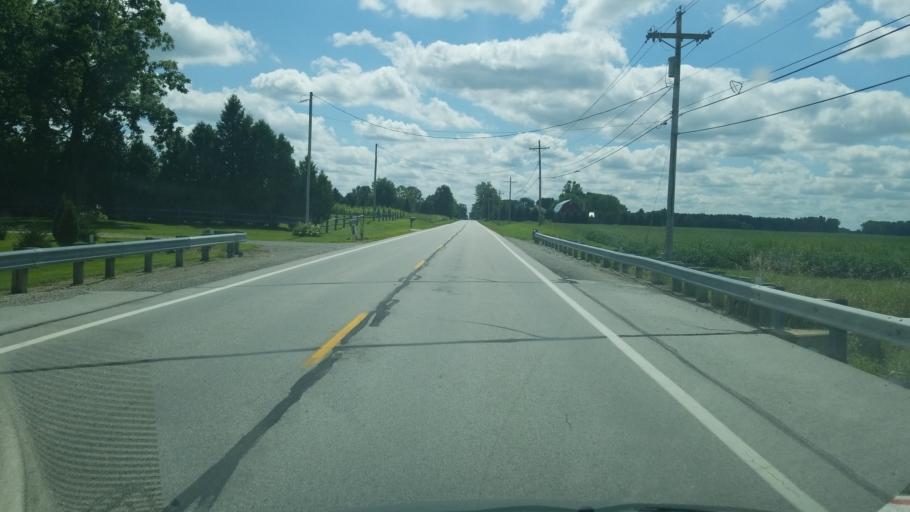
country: US
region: Ohio
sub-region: Henry County
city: Liberty Center
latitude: 41.5070
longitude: -84.0087
